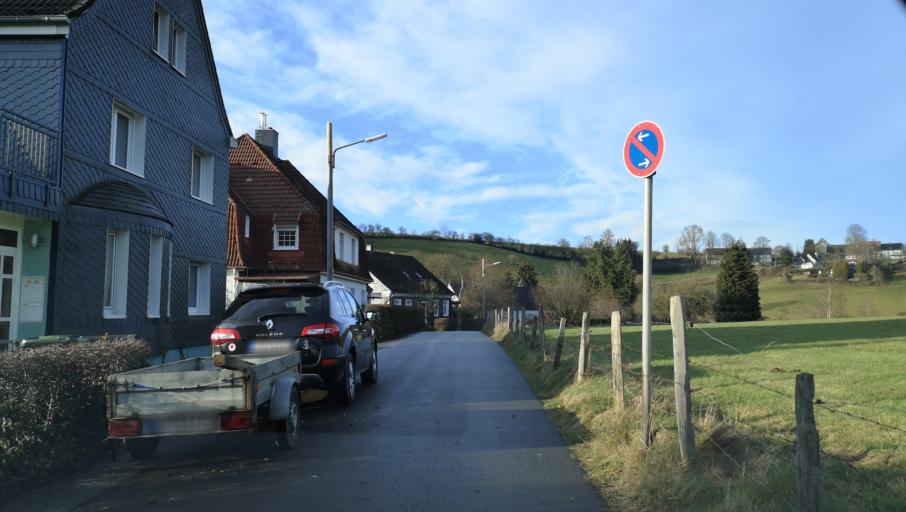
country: DE
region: North Rhine-Westphalia
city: Radevormwald
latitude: 51.2256
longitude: 7.3135
